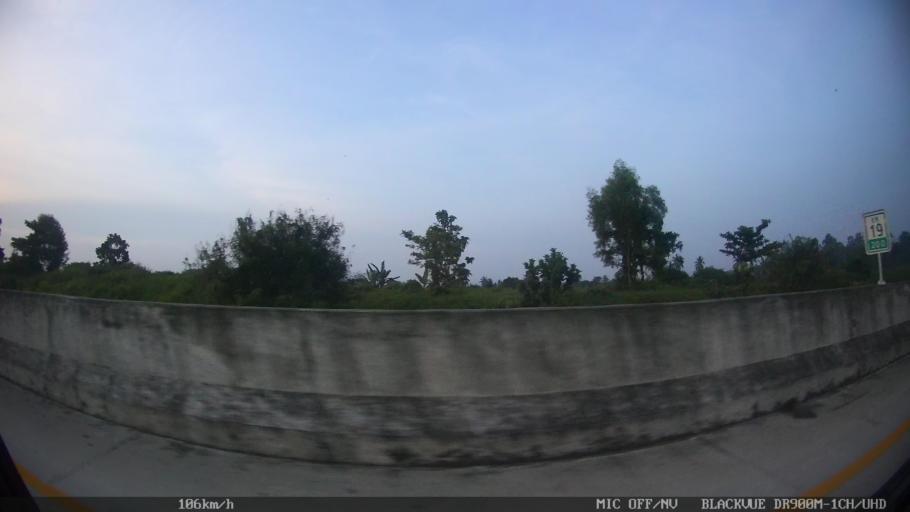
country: ID
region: Lampung
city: Pasuruan
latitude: -5.7317
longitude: 105.6796
